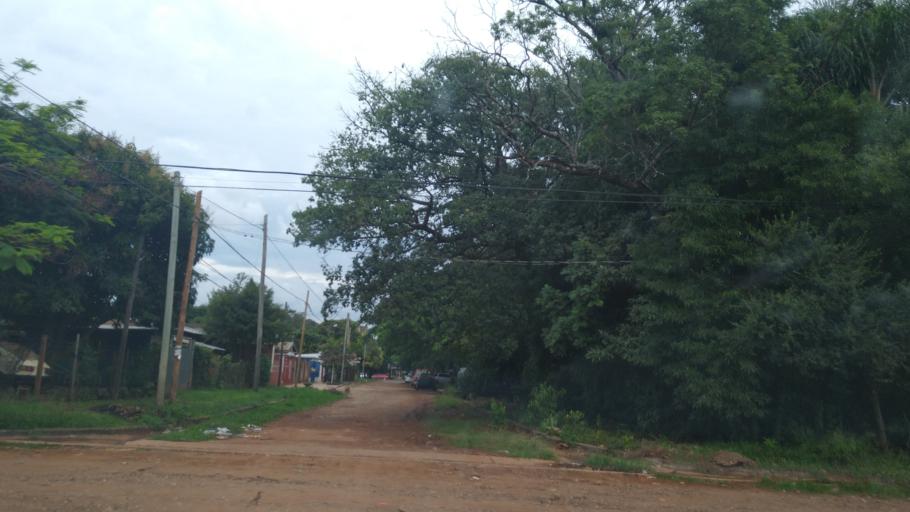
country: AR
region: Misiones
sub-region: Departamento de Capital
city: Posadas
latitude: -27.3730
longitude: -55.9271
